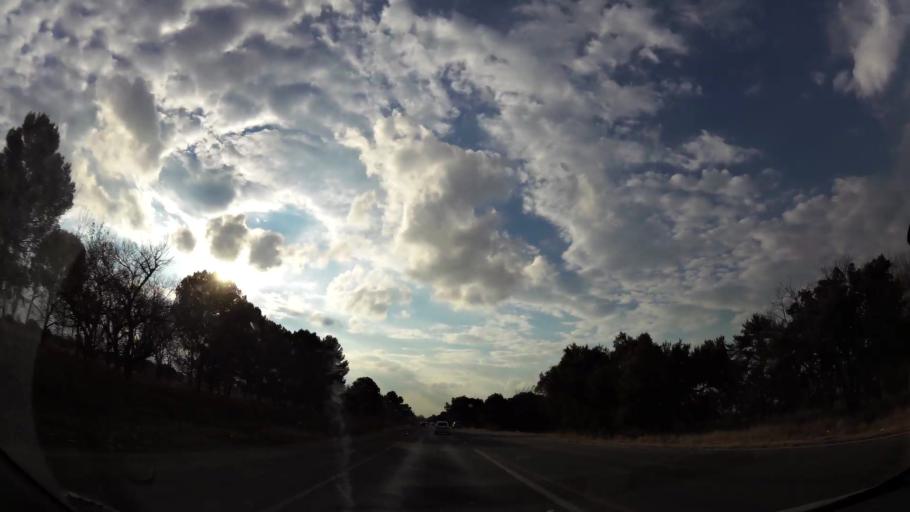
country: ZA
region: Orange Free State
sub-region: Fezile Dabi District Municipality
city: Sasolburg
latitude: -26.7964
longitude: 27.8300
